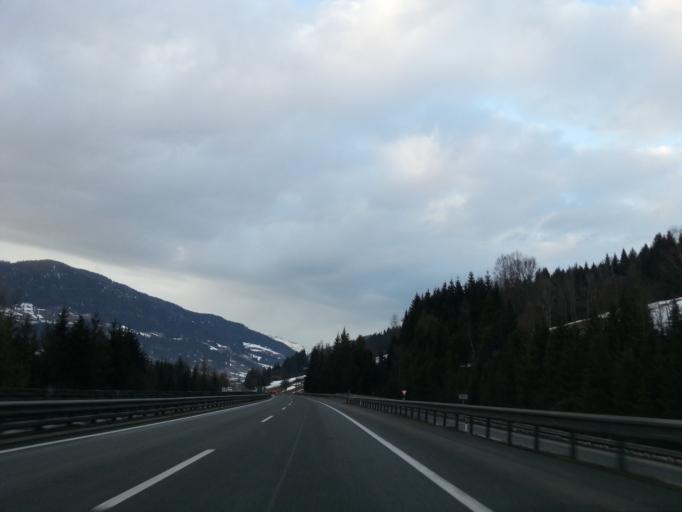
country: AT
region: Salzburg
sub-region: Politischer Bezirk Sankt Johann im Pongau
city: Flachau
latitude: 47.3599
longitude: 13.3980
